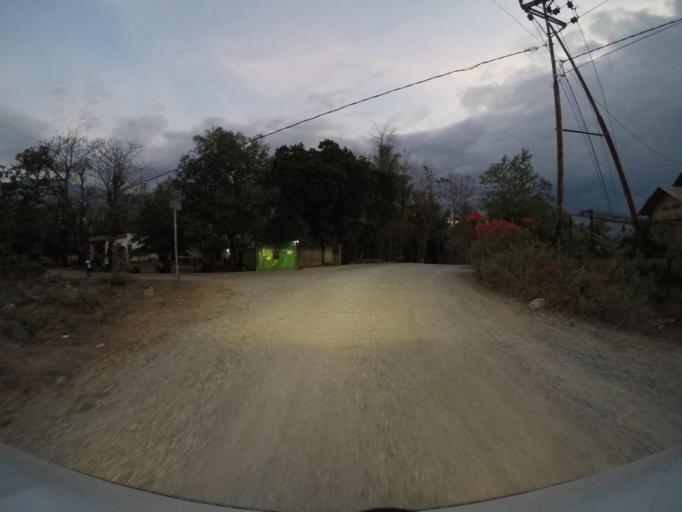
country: TL
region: Bobonaro
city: Maliana
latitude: -8.9799
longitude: 125.2185
